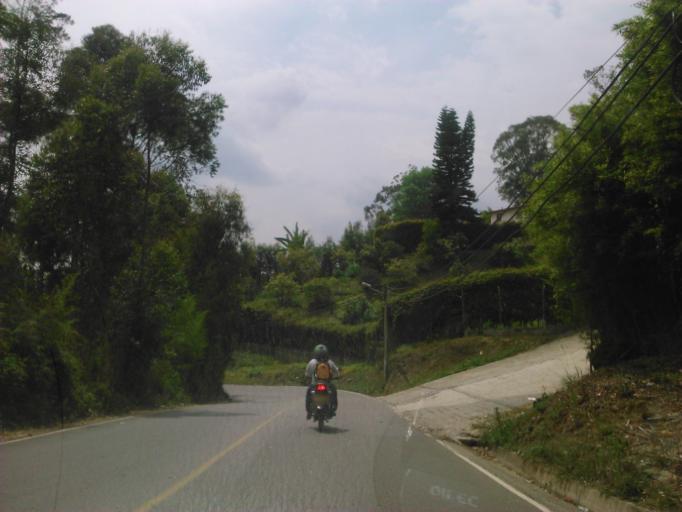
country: CO
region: Antioquia
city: San Vicente
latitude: 6.2255
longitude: -75.3909
